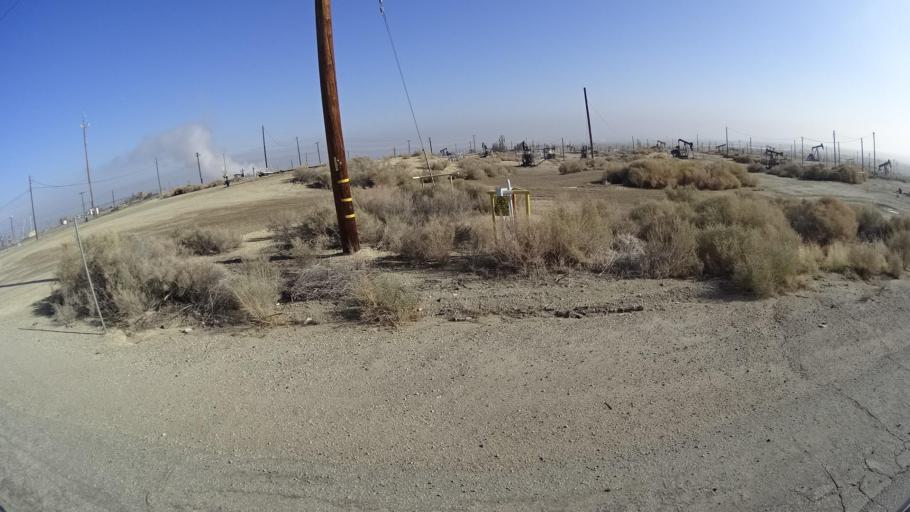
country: US
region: California
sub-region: Kern County
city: Taft Heights
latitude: 35.2019
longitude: -119.5933
